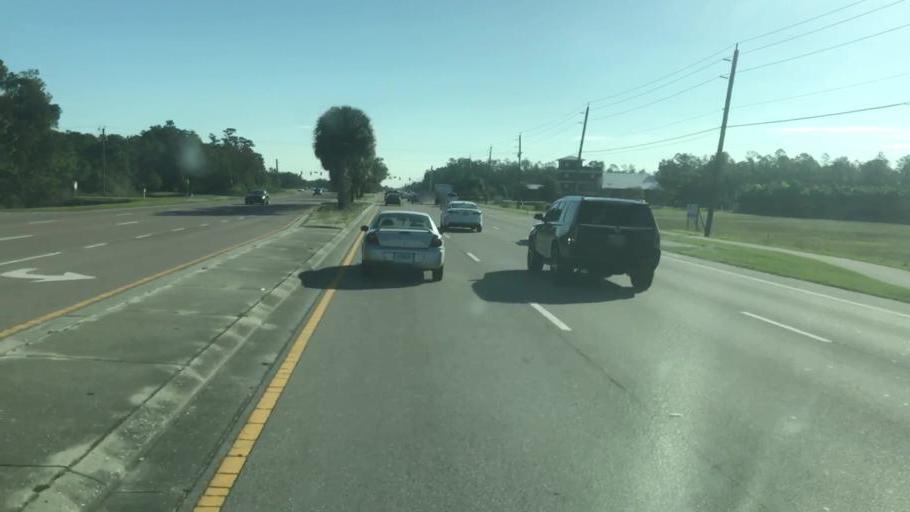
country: US
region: Florida
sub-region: Lee County
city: Villas
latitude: 26.5469
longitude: -81.8200
